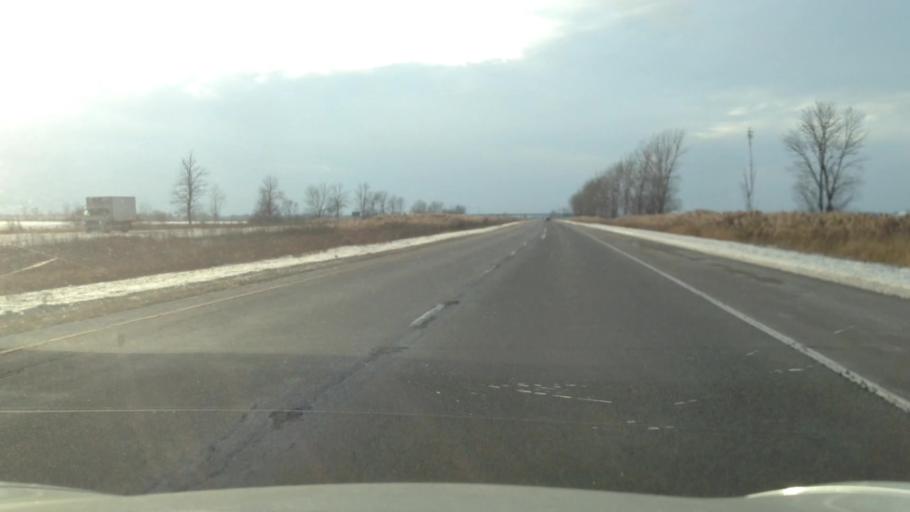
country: CA
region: Ontario
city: Casselman
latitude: 45.3287
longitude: -74.9702
